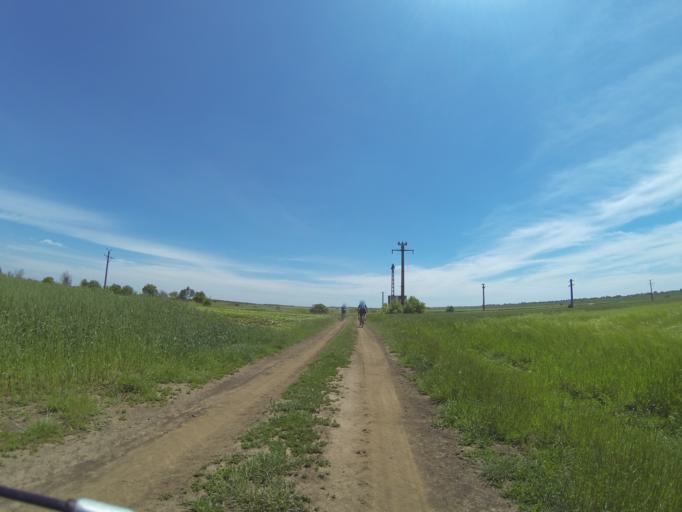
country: RO
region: Dolj
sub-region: Comuna Leu
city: Zanoaga
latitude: 44.1752
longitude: 24.0915
